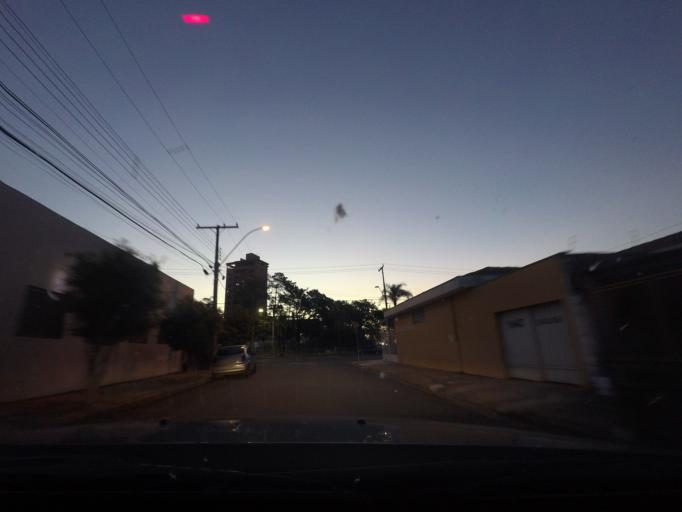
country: BR
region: Sao Paulo
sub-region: Piracicaba
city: Piracicaba
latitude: -22.7181
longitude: -47.6326
